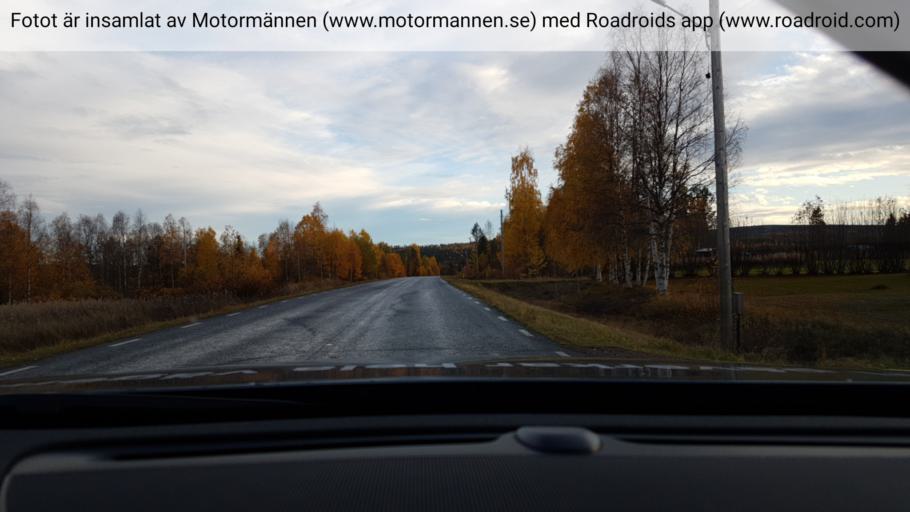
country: SE
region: Norrbotten
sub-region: Overkalix Kommun
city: OEverkalix
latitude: 66.9343
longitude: 22.7357
